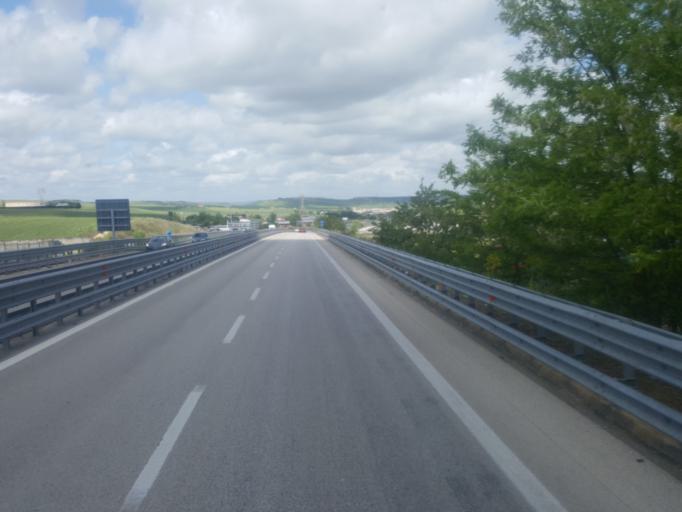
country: IT
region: Basilicate
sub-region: Provincia di Matera
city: Matera
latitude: 40.7044
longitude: 16.5842
